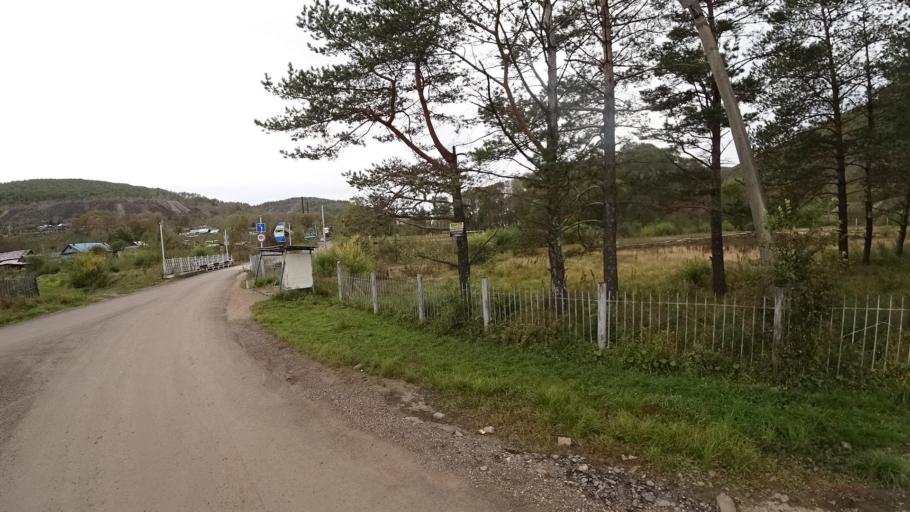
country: RU
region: Jewish Autonomous Oblast
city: Khingansk
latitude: 49.1289
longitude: 131.1981
